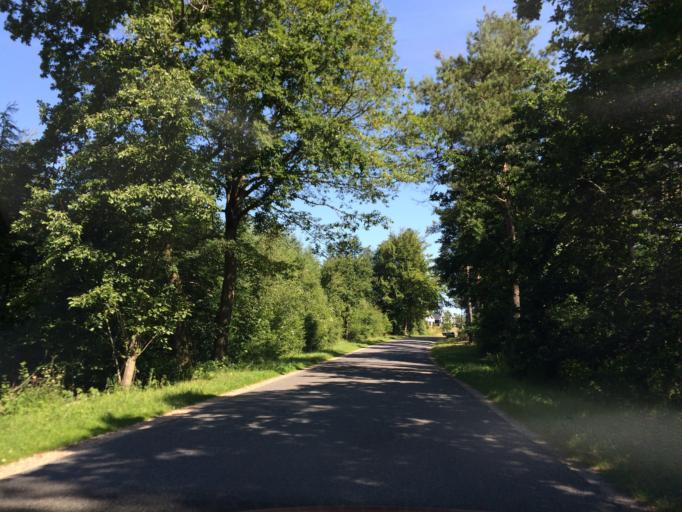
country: DK
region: Central Jutland
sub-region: Silkeborg Kommune
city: Svejbaek
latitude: 56.2142
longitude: 9.7223
